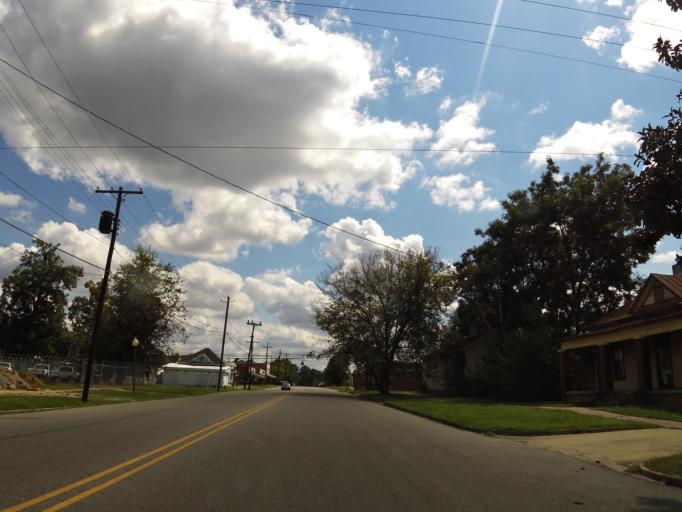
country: US
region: Alabama
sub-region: Dallas County
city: Selma
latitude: 32.4106
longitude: -87.0153
